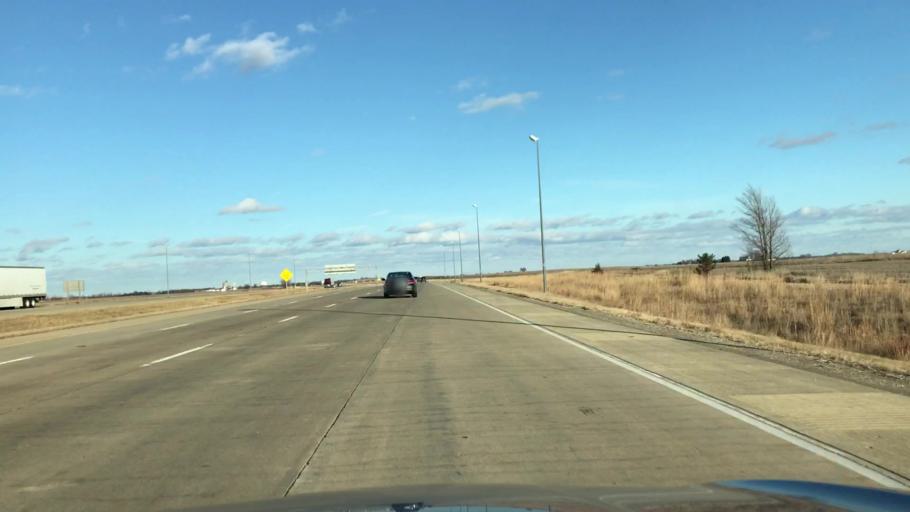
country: US
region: Illinois
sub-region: McLean County
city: Normal
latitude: 40.5386
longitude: -88.9413
